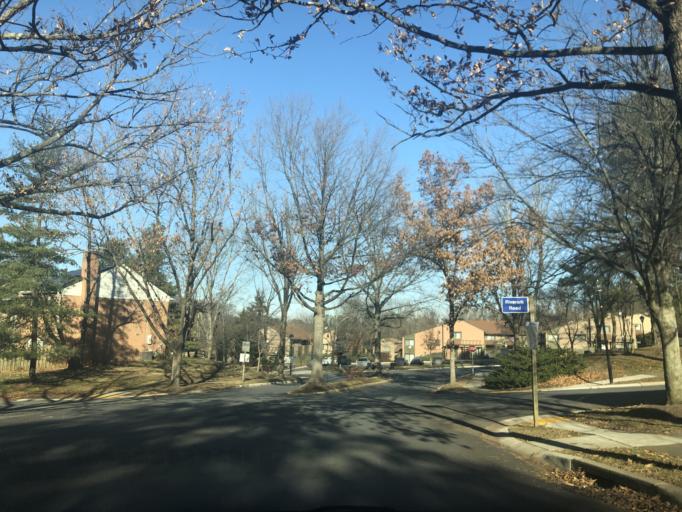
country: US
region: Maryland
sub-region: Howard County
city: Columbia
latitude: 39.2113
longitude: -76.8405
